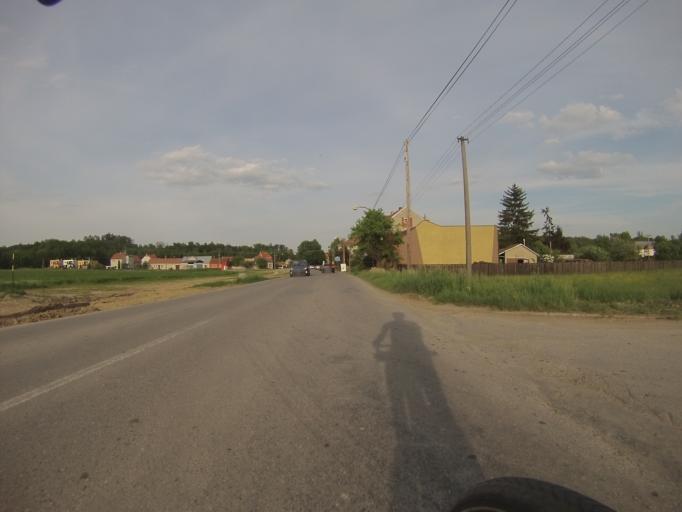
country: CZ
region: Olomoucky
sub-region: Okres Prostejov
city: Plumlov
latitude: 49.4622
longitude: 16.9928
